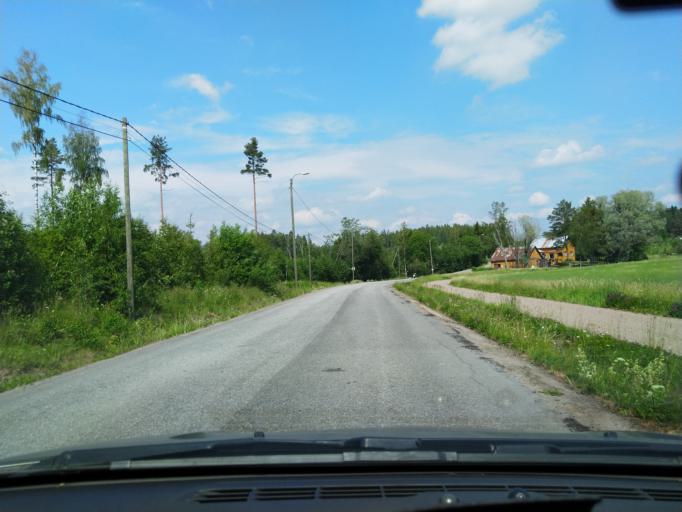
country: FI
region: Uusimaa
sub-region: Helsinki
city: Saukkola
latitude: 60.3722
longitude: 24.1065
